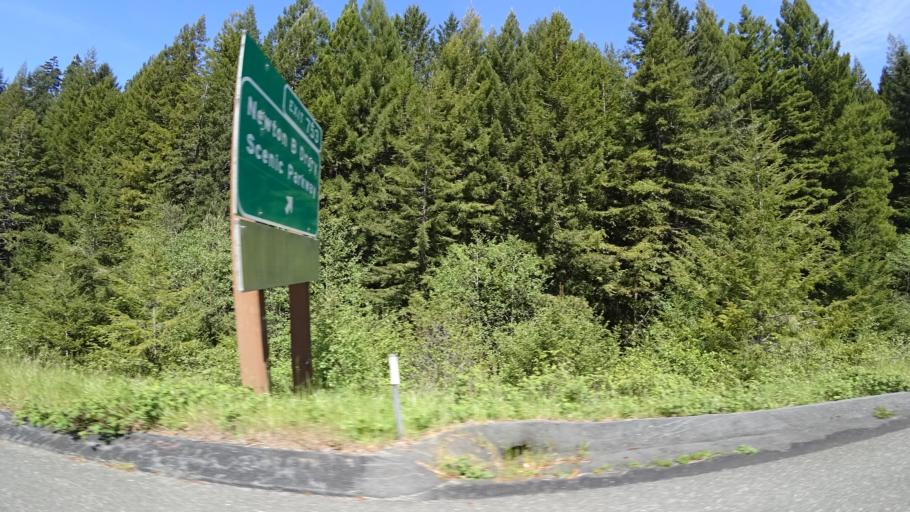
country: US
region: California
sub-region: Humboldt County
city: Westhaven-Moonstone
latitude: 41.3516
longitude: -124.0226
